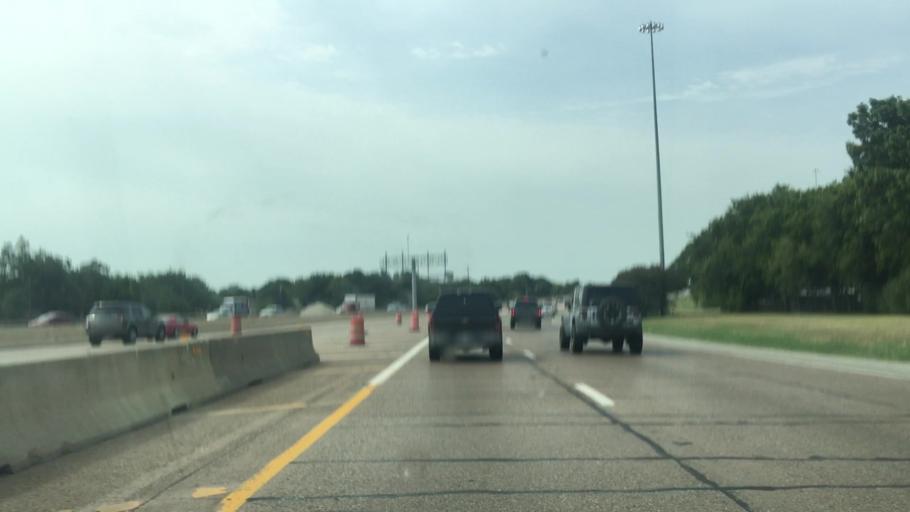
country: US
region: Texas
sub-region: Dallas County
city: Cockrell Hill
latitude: 32.7096
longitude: -96.8295
